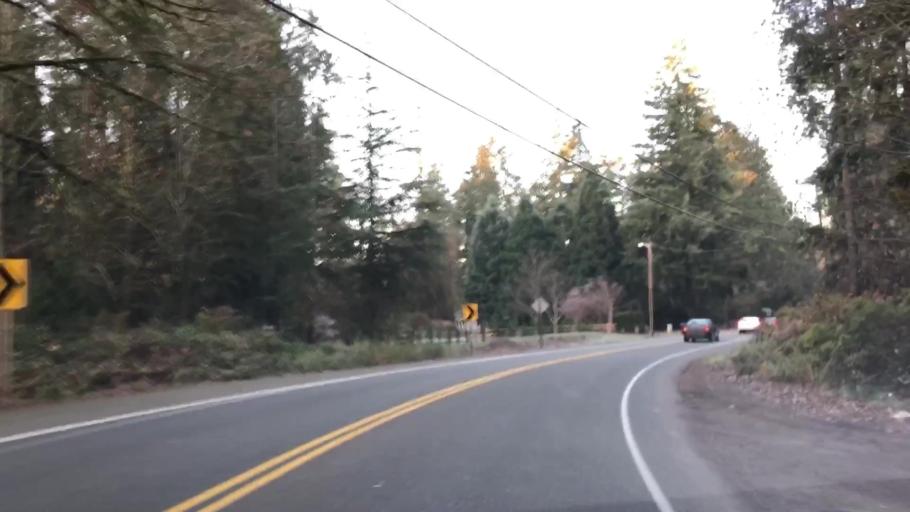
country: US
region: Washington
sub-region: King County
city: Cottage Lake
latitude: 47.7175
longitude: -122.0828
